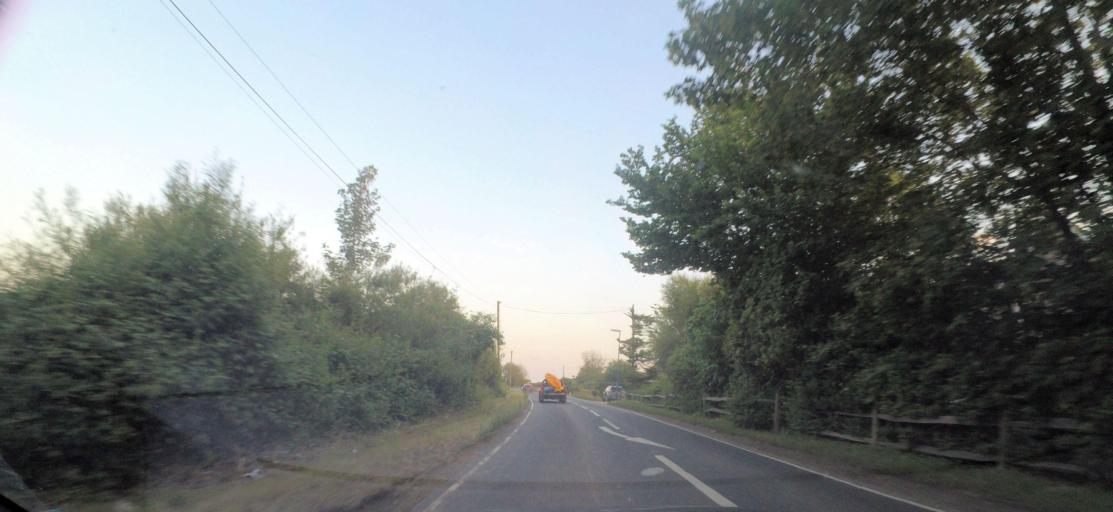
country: GB
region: England
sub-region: West Sussex
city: Selsey
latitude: 50.7526
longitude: -0.7821
